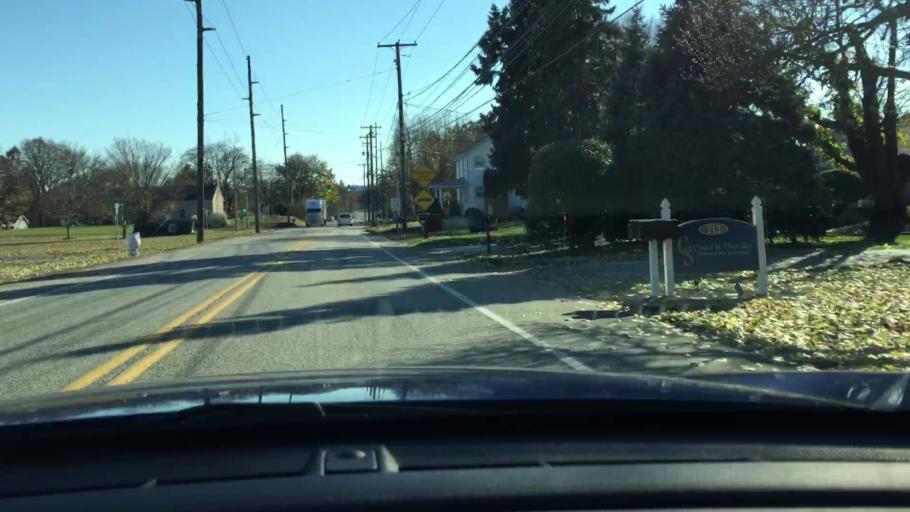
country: US
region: Pennsylvania
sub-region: Cumberland County
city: Shiremanstown
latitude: 40.2333
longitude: -76.9717
